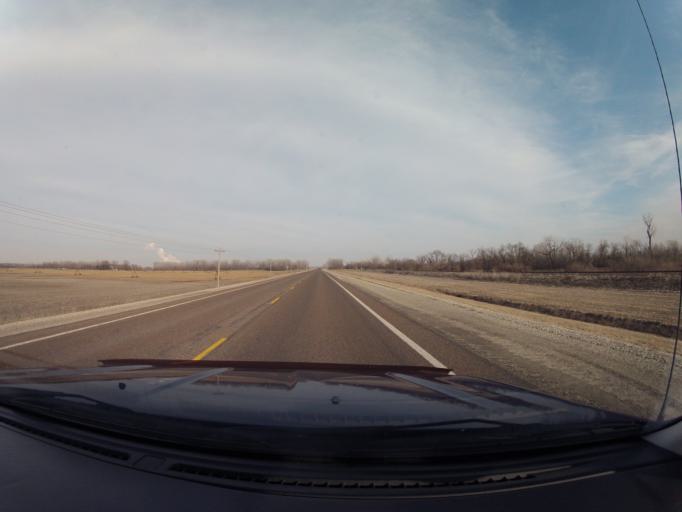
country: US
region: Kansas
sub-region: Pottawatomie County
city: Wamego
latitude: 39.2116
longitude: -96.2449
